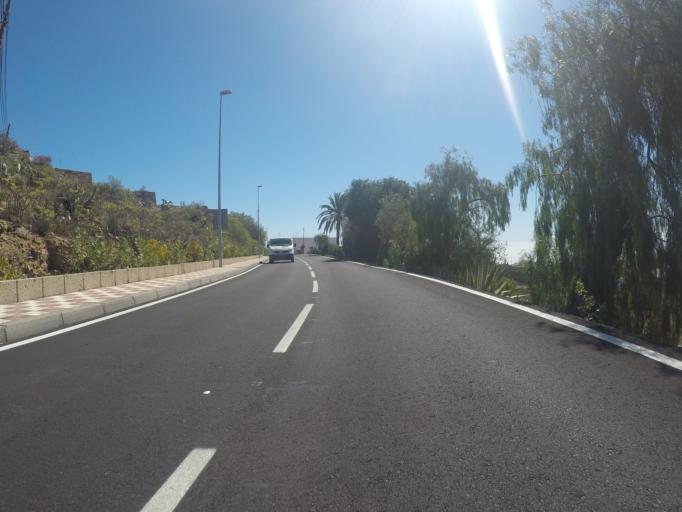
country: ES
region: Canary Islands
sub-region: Provincia de Santa Cruz de Tenerife
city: Lomo de Arico
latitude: 28.1801
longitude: -16.4822
